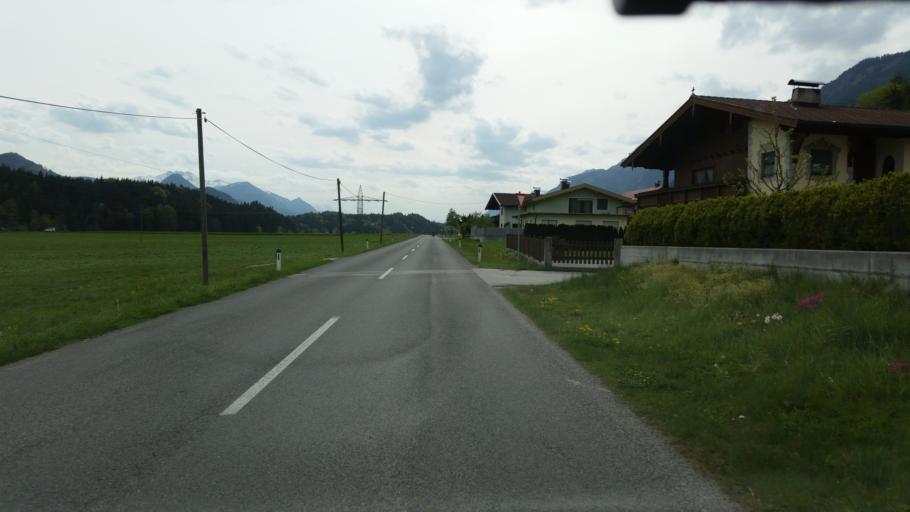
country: AT
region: Tyrol
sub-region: Politischer Bezirk Kufstein
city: Radfeld
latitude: 47.4746
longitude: 11.9368
